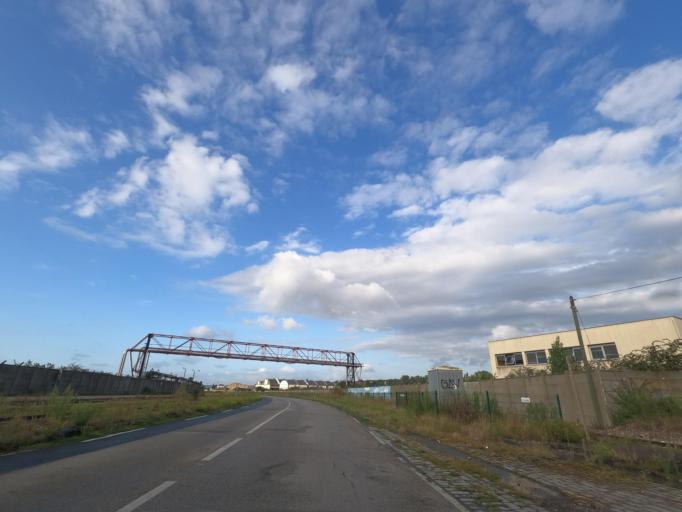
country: FR
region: Haute-Normandie
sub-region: Departement de la Seine-Maritime
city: Petit-Couronne
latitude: 49.3796
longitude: 1.0135
